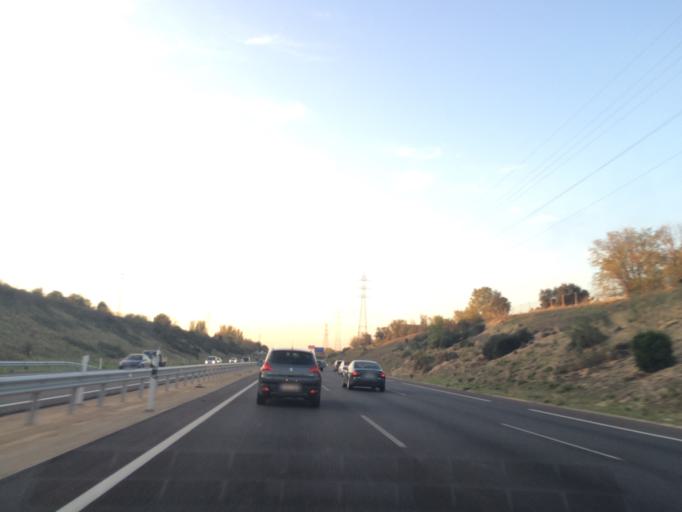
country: ES
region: Madrid
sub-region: Provincia de Madrid
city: Pozuelo de Alarcon
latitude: 40.4415
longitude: -3.8489
